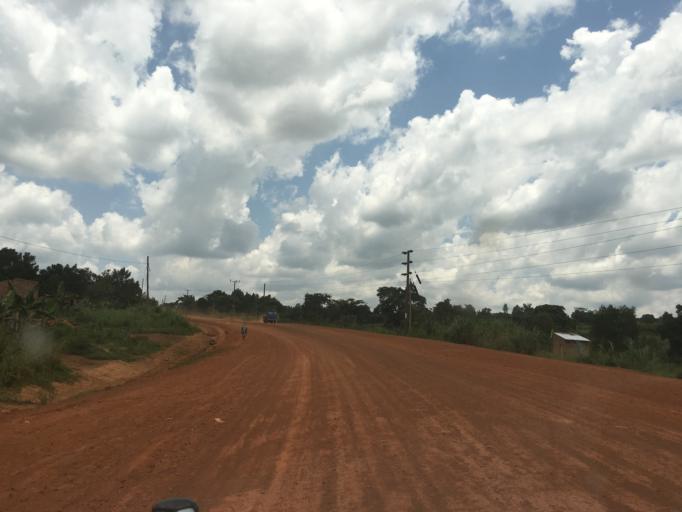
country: UG
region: Western Region
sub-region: Kibale District
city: Kagadi
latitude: 1.1685
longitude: 31.0270
